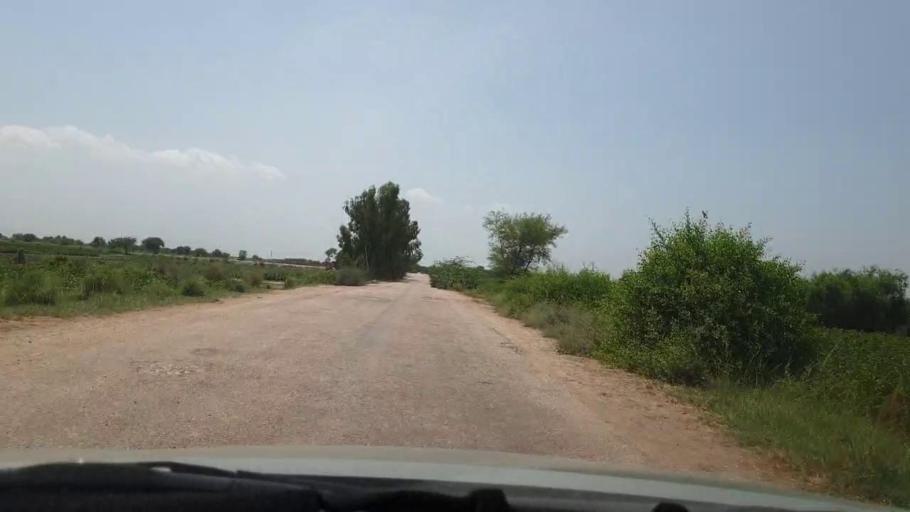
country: PK
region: Sindh
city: Rohri
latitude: 27.6696
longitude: 69.0820
